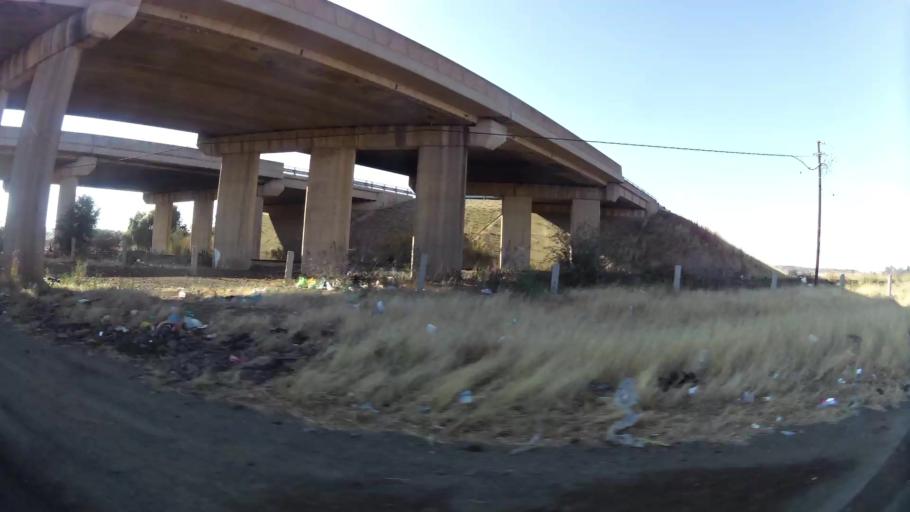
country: ZA
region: Orange Free State
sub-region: Mangaung Metropolitan Municipality
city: Bloemfontein
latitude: -29.1807
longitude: 26.1895
